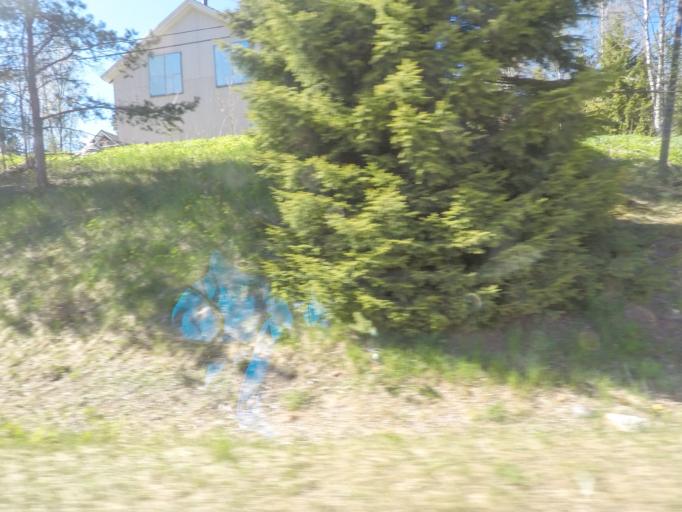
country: FI
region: Uusimaa
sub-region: Helsinki
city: Sammatti
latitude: 60.3672
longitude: 23.8093
